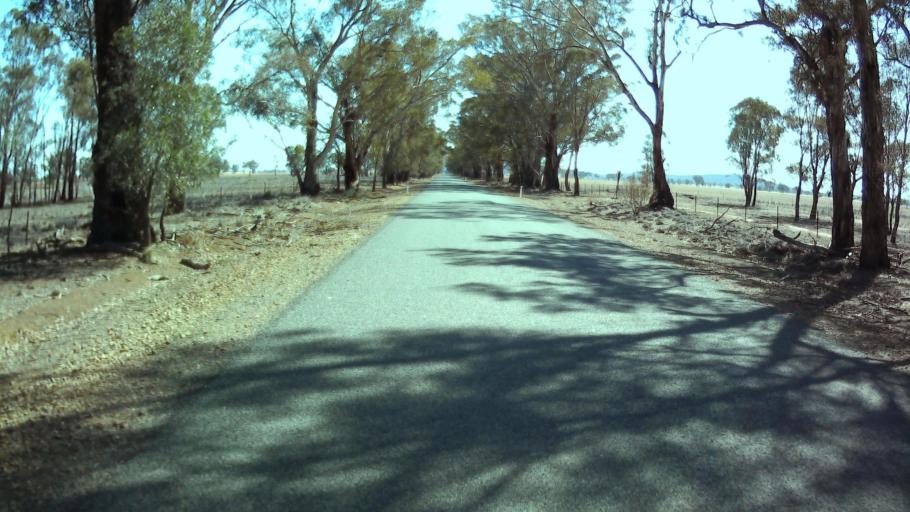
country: AU
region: New South Wales
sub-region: Weddin
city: Grenfell
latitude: -33.7246
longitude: 147.8952
